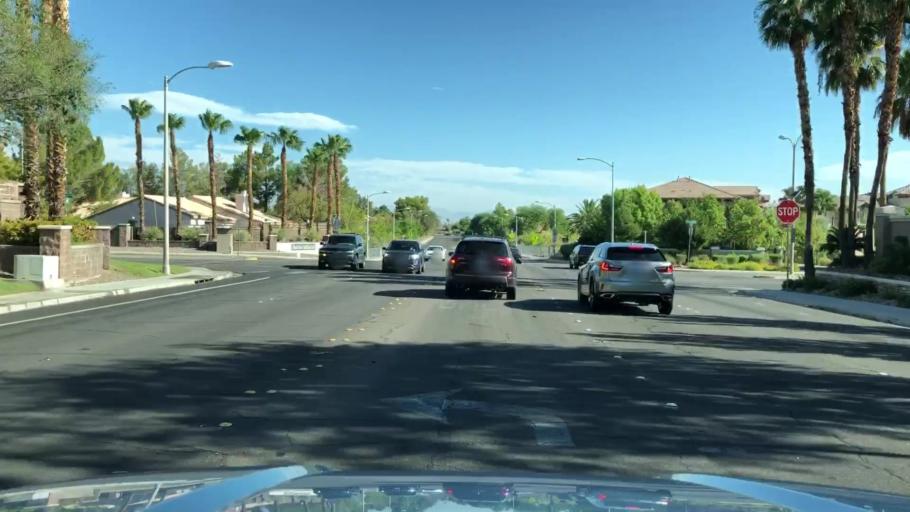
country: US
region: Nevada
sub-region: Clark County
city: Whitney
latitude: 36.0412
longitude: -115.0687
